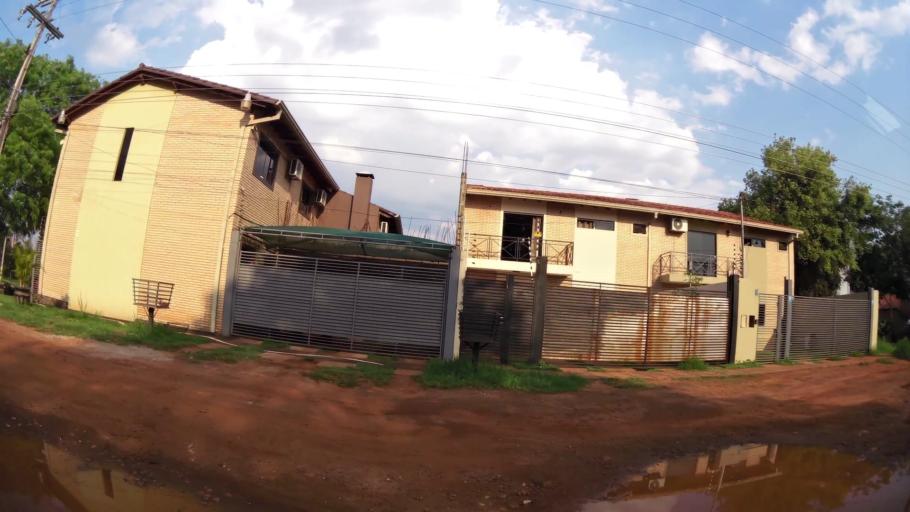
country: PY
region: Alto Parana
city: Presidente Franco
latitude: -25.5204
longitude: -54.6264
